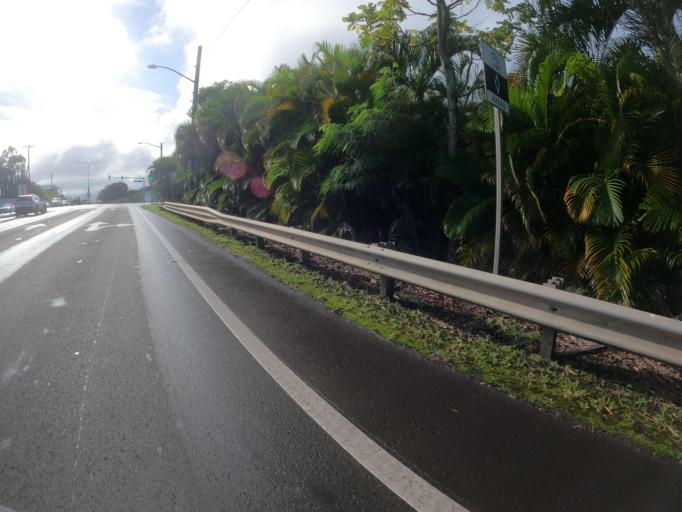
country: US
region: Hawaii
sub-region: Honolulu County
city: He'eia
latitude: 21.4173
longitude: -157.8139
